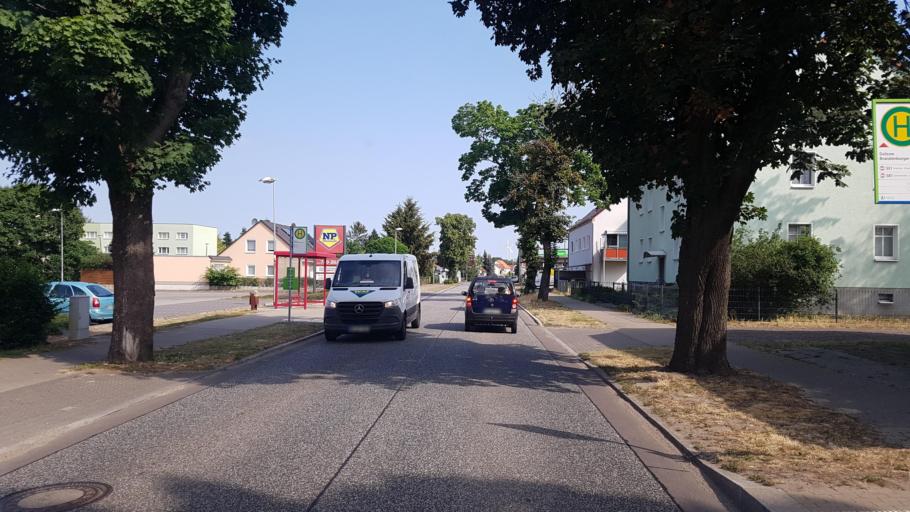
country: DE
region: Brandenburg
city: Golzow
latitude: 52.2828
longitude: 12.6033
